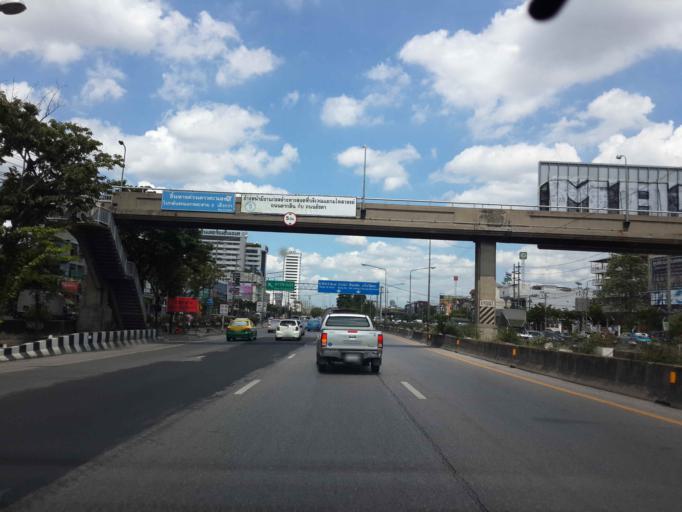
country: TH
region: Bangkok
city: Chom Thong
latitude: 13.6804
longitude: 100.4717
